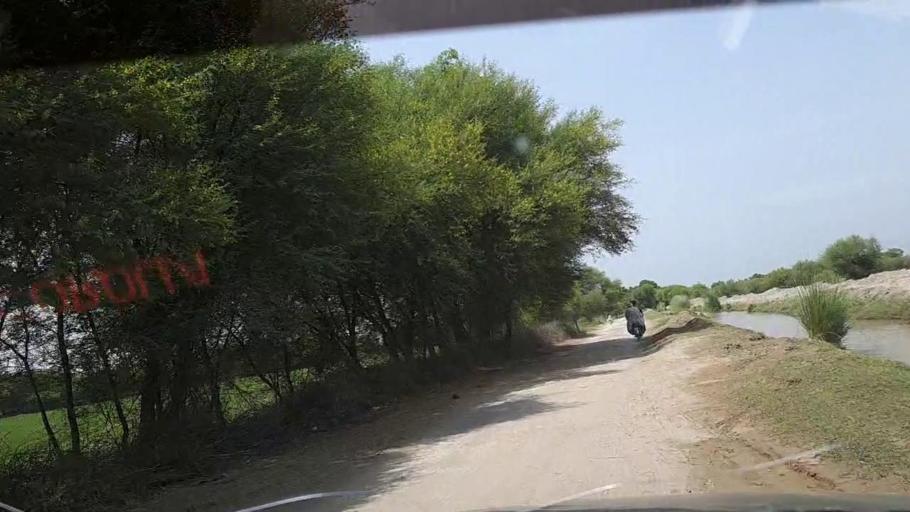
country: PK
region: Sindh
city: Khanpur
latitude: 27.8156
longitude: 69.4487
